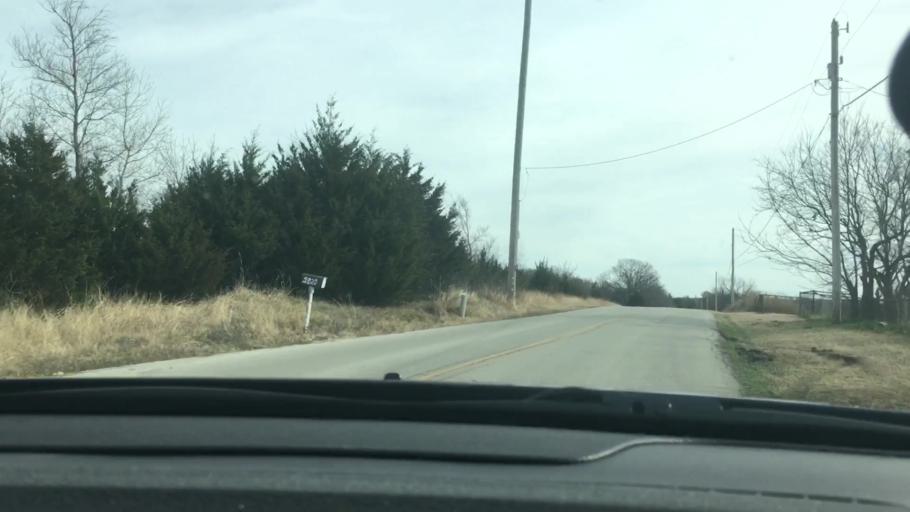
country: US
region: Oklahoma
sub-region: Carter County
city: Ardmore
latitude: 34.1756
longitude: -97.0868
